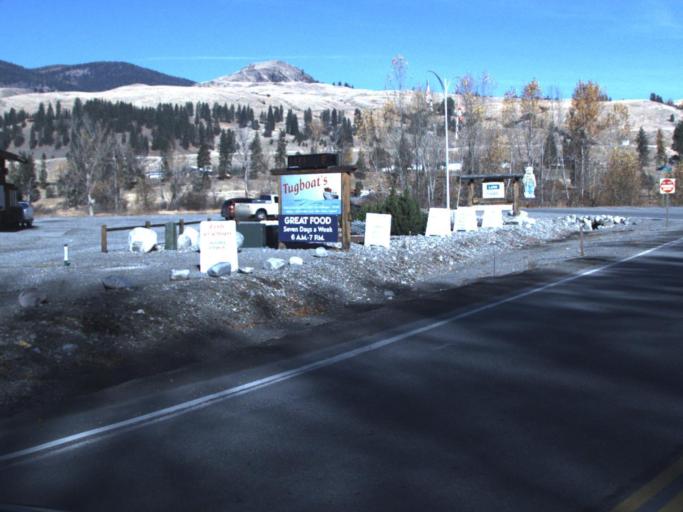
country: CA
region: British Columbia
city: Grand Forks
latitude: 48.8791
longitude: -118.6044
